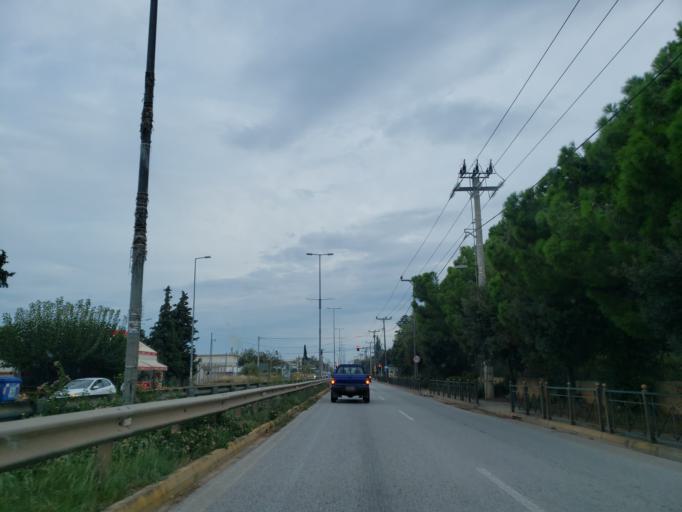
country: GR
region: Attica
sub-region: Nomarchia Anatolikis Attikis
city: Nea Makri
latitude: 38.1001
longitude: 23.9710
